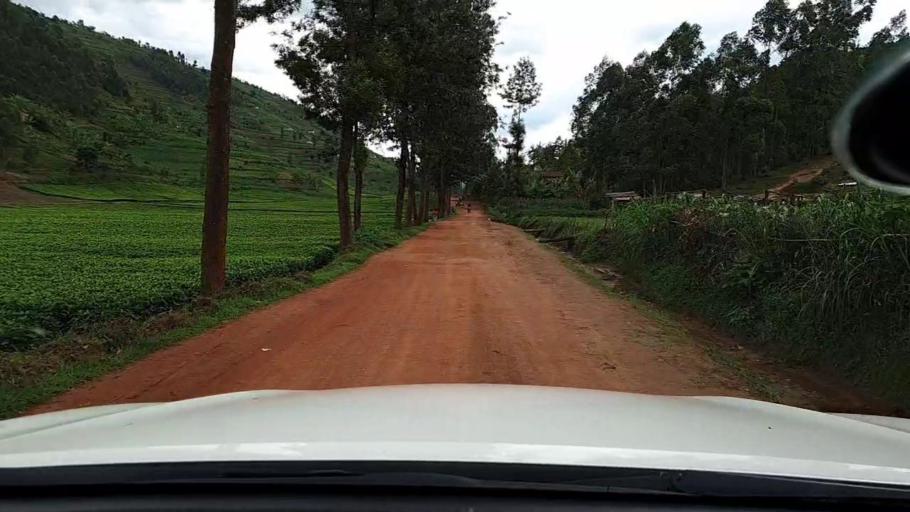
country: RW
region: Northern Province
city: Byumba
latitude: -1.6596
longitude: 29.9130
